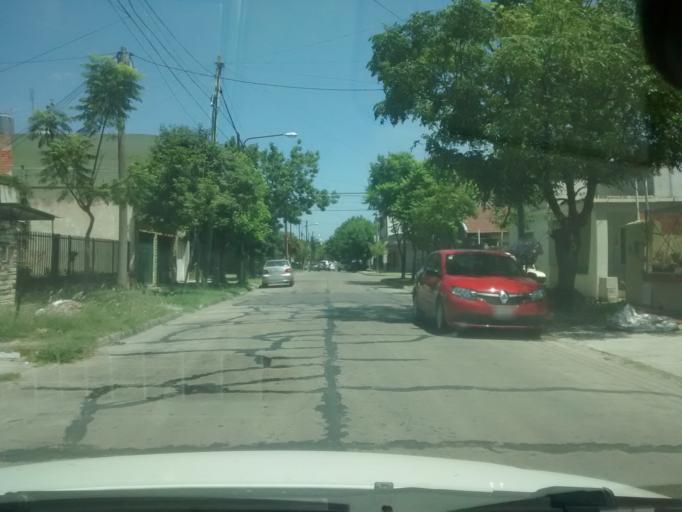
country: AR
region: Buenos Aires
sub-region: Partido de Moron
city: Moron
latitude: -34.6621
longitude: -58.6061
